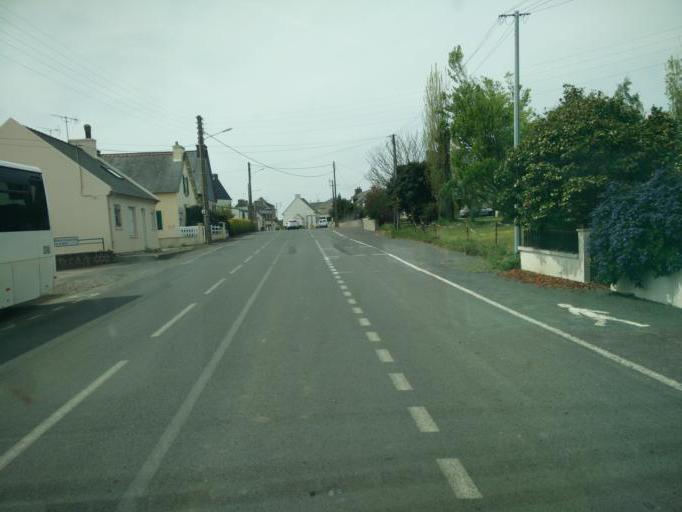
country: FR
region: Brittany
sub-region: Departement des Cotes-d'Armor
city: Matignon
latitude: 48.5942
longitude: -2.2846
